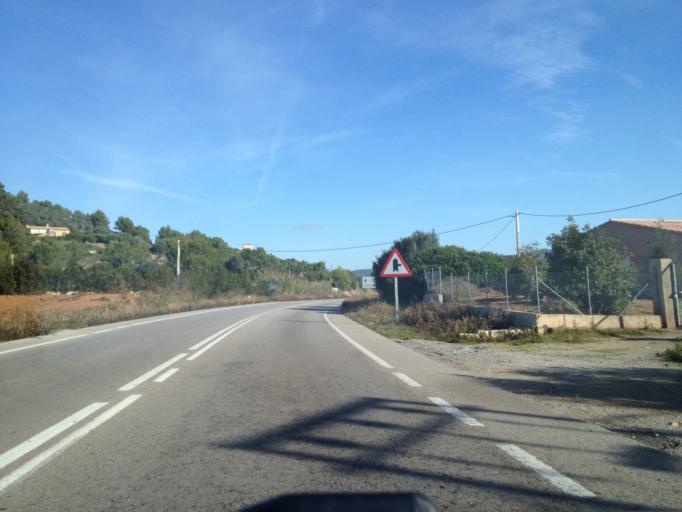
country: ES
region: Balearic Islands
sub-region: Illes Balears
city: Son Servera
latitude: 39.6360
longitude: 3.3670
